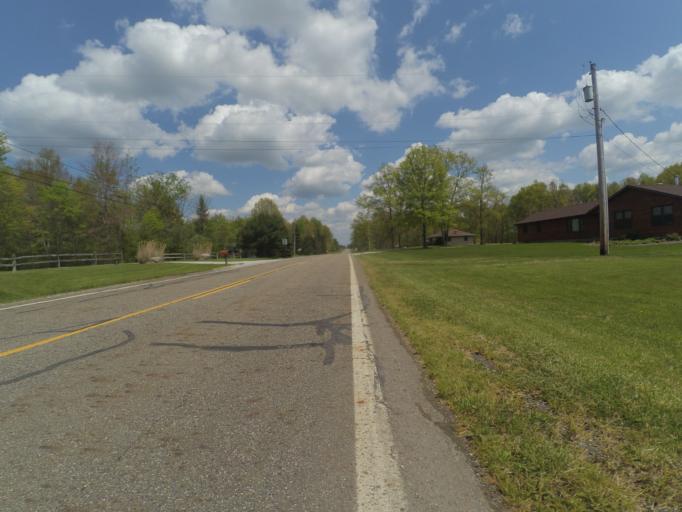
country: US
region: Ohio
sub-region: Mahoning County
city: Craig Beach
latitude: 41.1338
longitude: -81.0807
